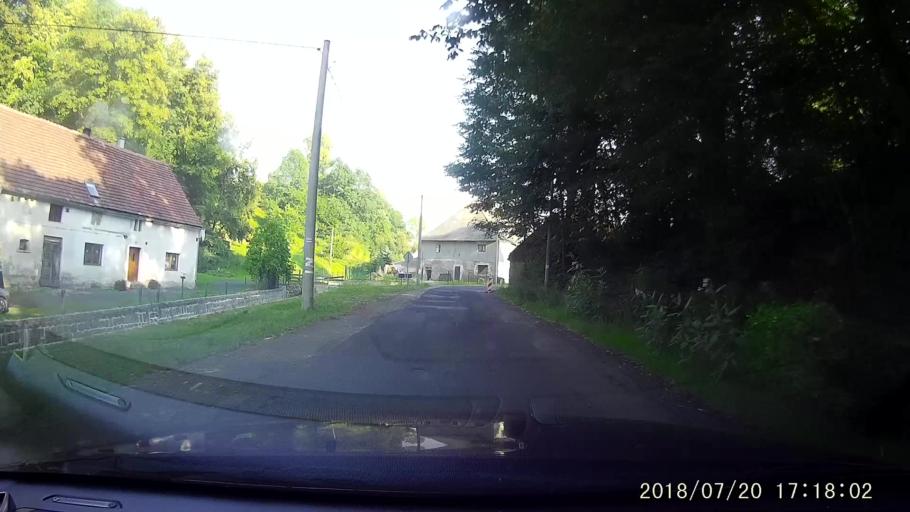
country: PL
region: Lower Silesian Voivodeship
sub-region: Powiat lubanski
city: Lesna
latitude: 50.9959
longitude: 15.2859
